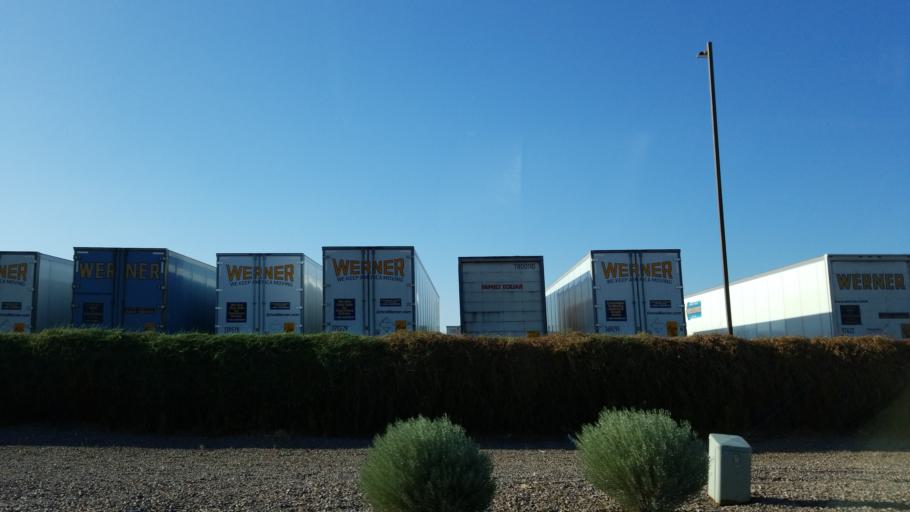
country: US
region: Arizona
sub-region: Maricopa County
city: Laveen
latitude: 33.4224
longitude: -112.1632
